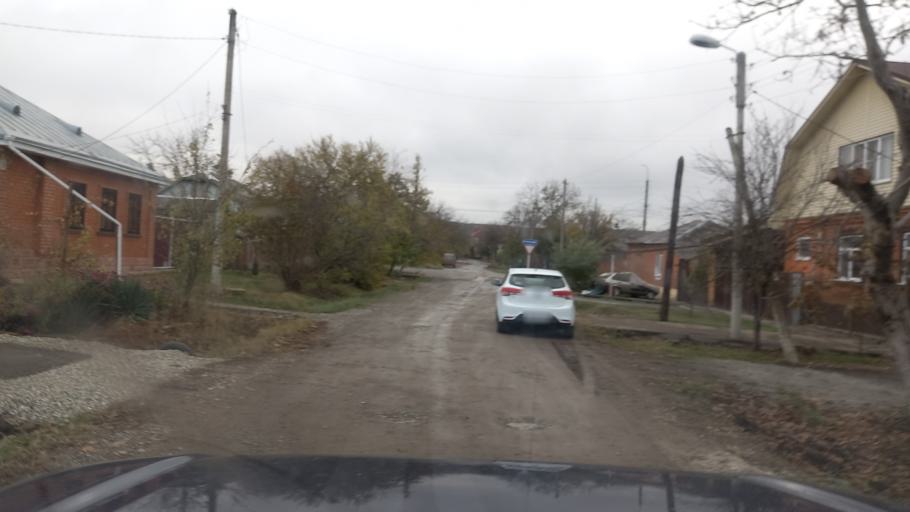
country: RU
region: Adygeya
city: Maykop
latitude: 44.6035
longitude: 40.0854
